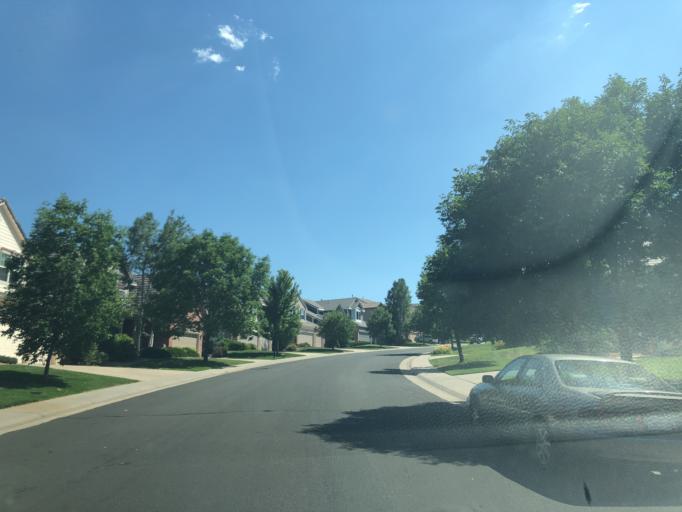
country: US
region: Colorado
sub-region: Arapahoe County
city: Dove Valley
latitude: 39.6077
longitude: -104.7818
